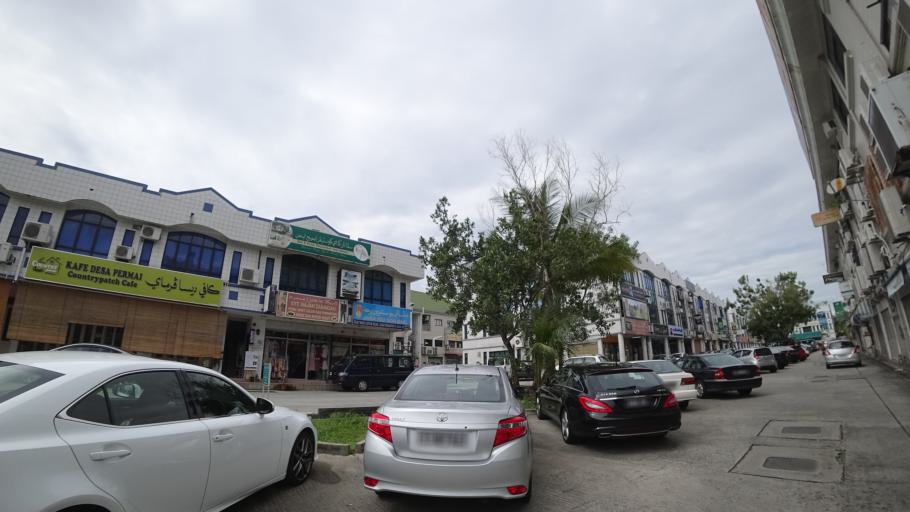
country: BN
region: Brunei and Muara
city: Bandar Seri Begawan
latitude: 4.9002
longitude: 114.9266
